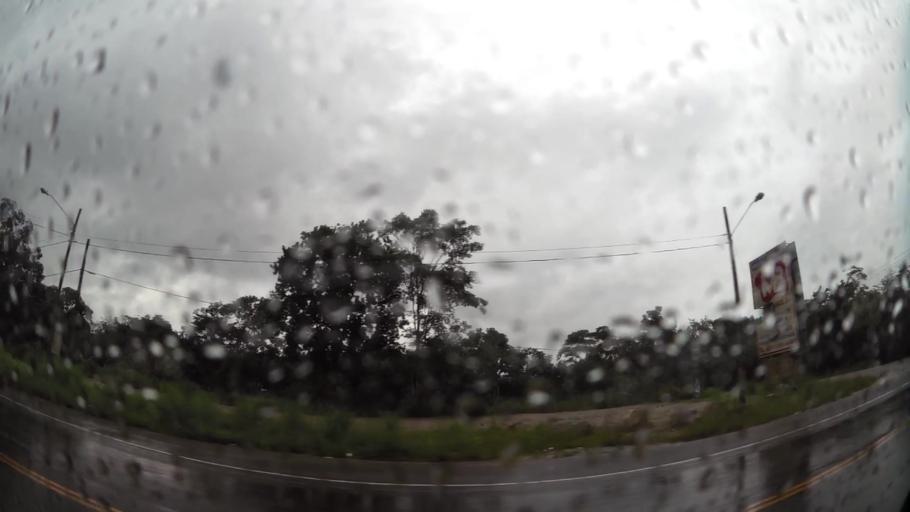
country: PA
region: Colon
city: Quebrada Bonita Adentro
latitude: 9.2852
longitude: -79.7153
